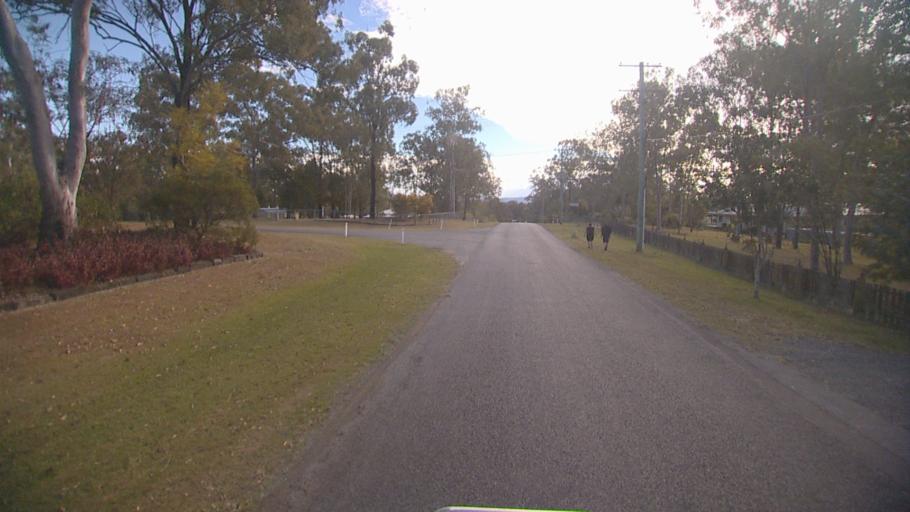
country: AU
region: Queensland
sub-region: Logan
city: North Maclean
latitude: -27.8185
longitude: 153.0535
